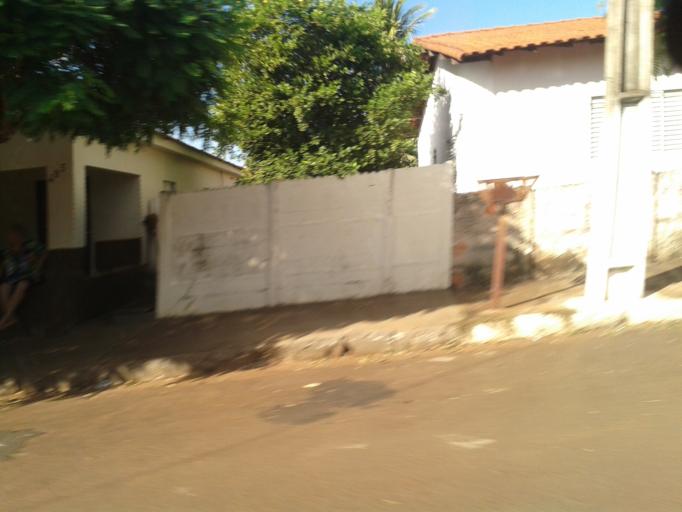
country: BR
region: Minas Gerais
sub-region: Santa Vitoria
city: Santa Vitoria
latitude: -18.6948
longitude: -49.9416
